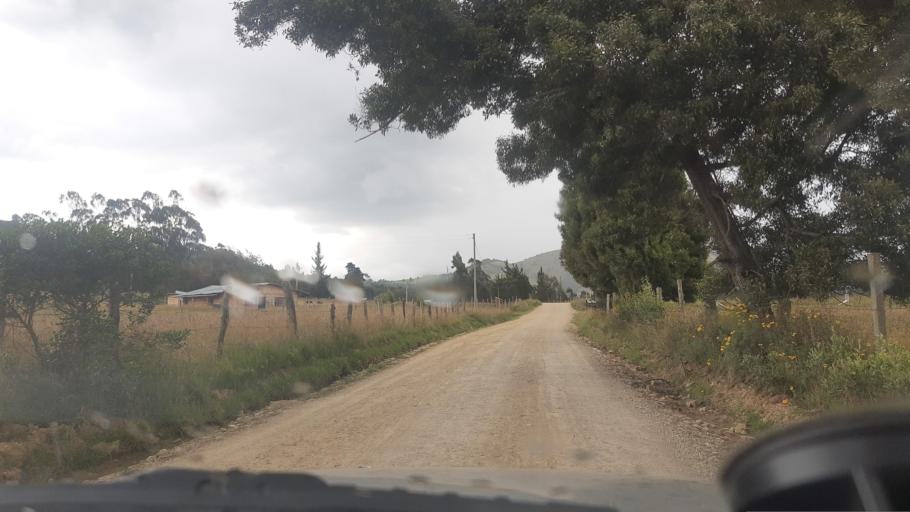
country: CO
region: Cundinamarca
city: Cucunuba
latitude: 5.1856
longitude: -73.7980
